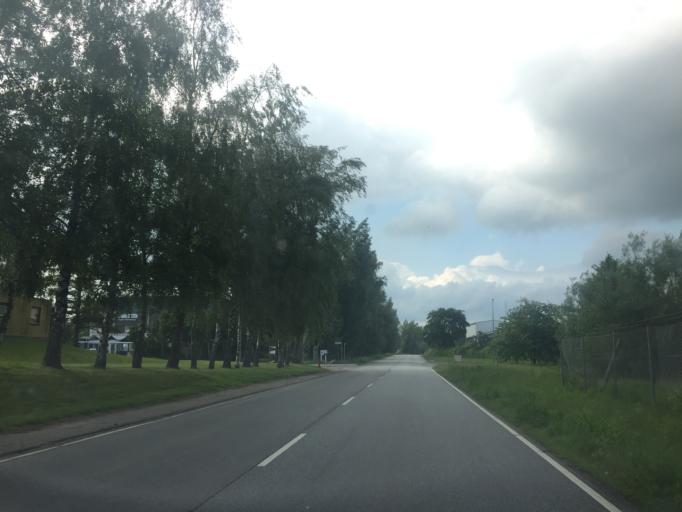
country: DK
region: Zealand
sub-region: Roskilde Kommune
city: Jyllinge
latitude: 55.7630
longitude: 12.1353
